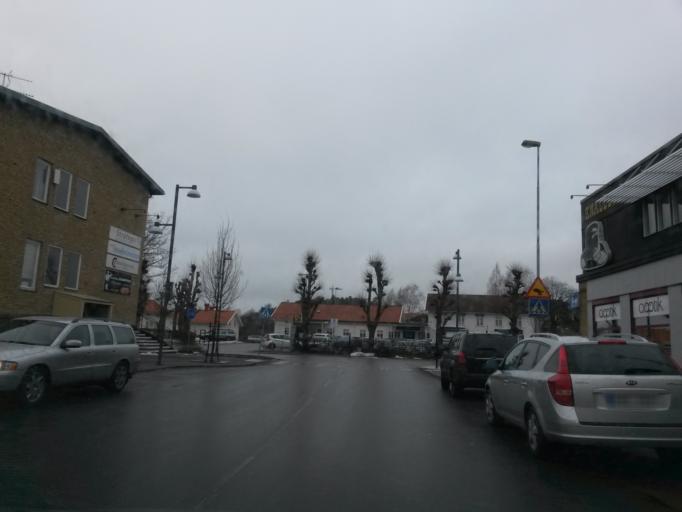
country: SE
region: Vaestra Goetaland
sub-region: Marks Kommun
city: Kinna
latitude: 57.5066
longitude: 12.6913
